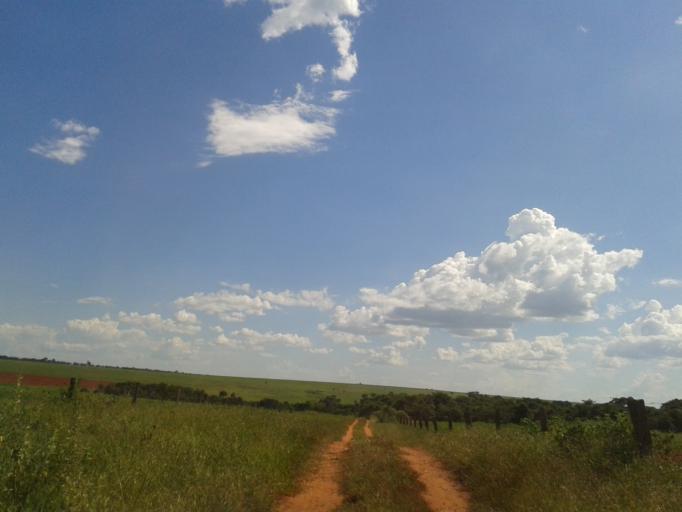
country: BR
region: Minas Gerais
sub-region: Santa Vitoria
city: Santa Vitoria
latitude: -19.1161
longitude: -50.5003
